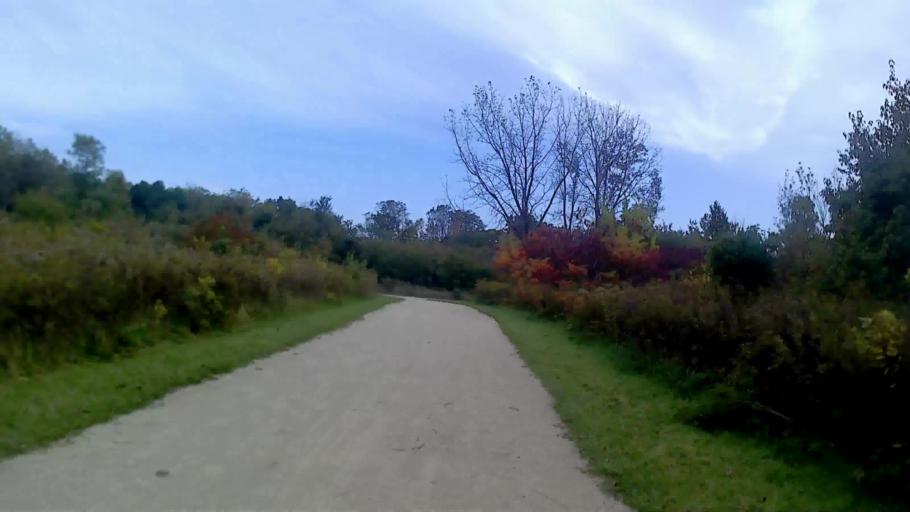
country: US
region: Illinois
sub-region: DuPage County
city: Naperville
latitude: 41.8111
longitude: -88.1414
